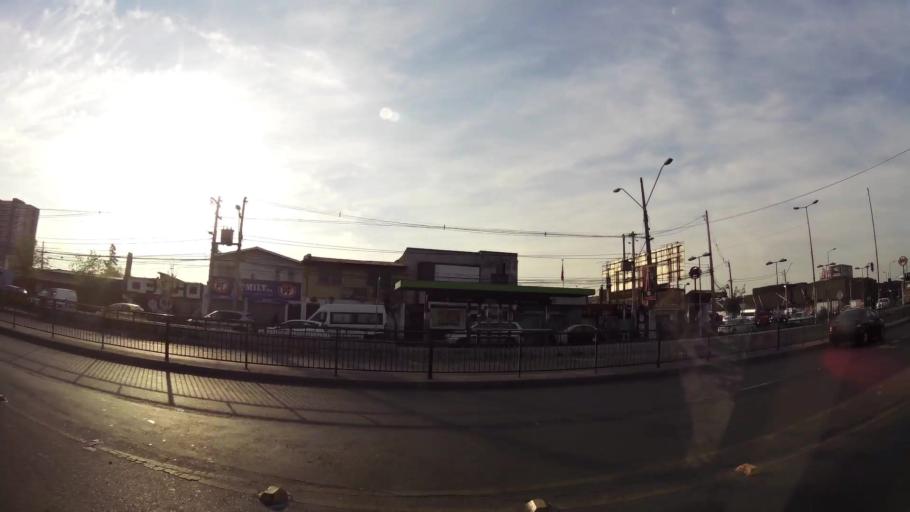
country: CL
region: Santiago Metropolitan
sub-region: Provincia de Santiago
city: La Pintana
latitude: -33.5364
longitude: -70.6644
